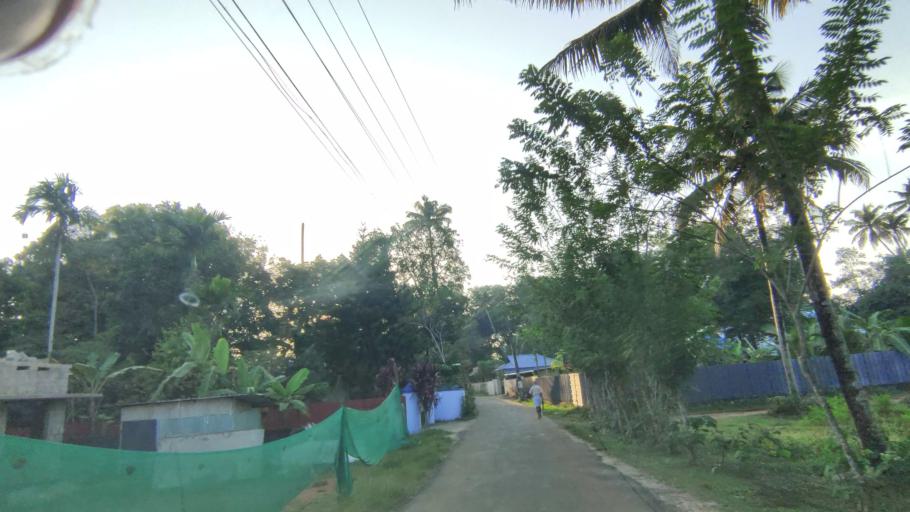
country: IN
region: Kerala
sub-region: Alappuzha
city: Shertallai
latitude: 9.6474
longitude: 76.3378
